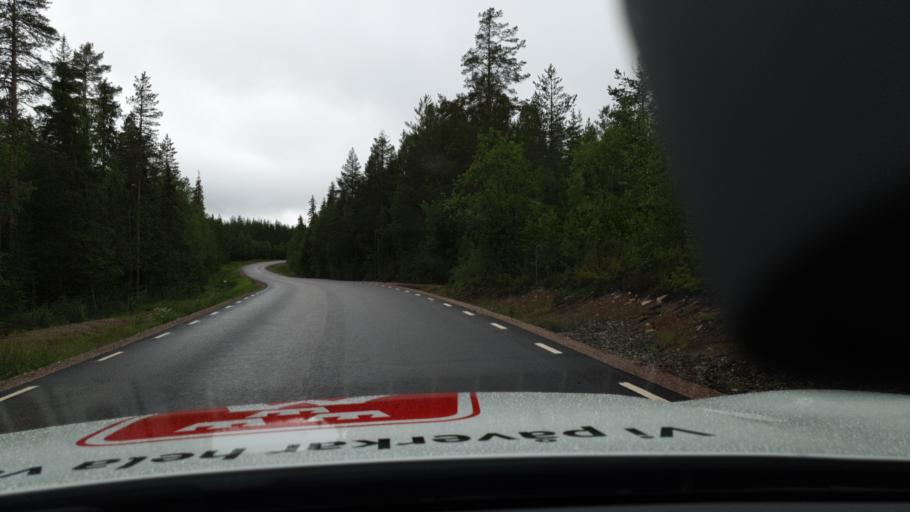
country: SE
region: Norrbotten
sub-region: Overtornea Kommun
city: OEvertornea
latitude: 66.4258
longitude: 23.5374
